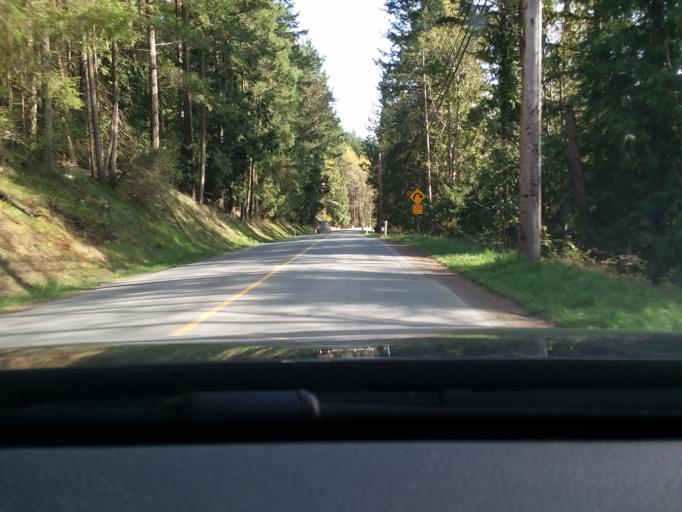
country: CA
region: British Columbia
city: North Saanich
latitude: 48.7832
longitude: -123.2802
